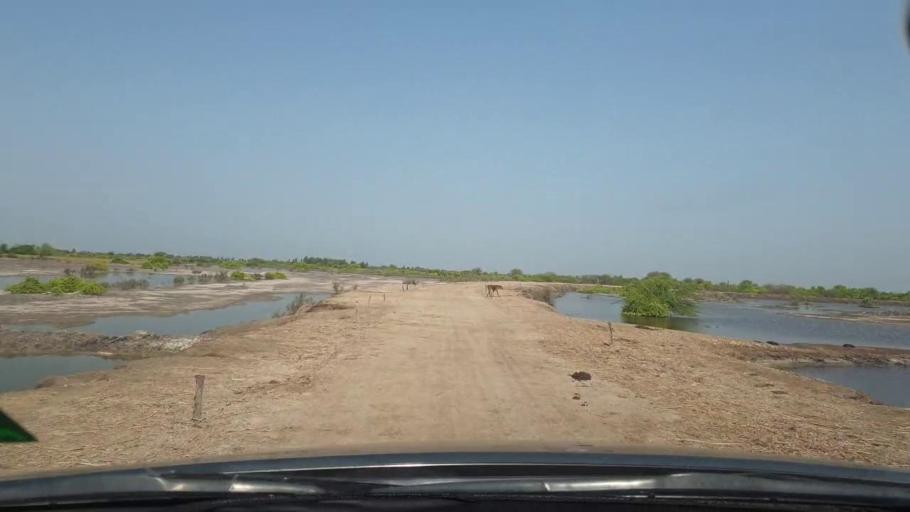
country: PK
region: Sindh
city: Tando Bago
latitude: 24.8036
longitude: 69.1084
